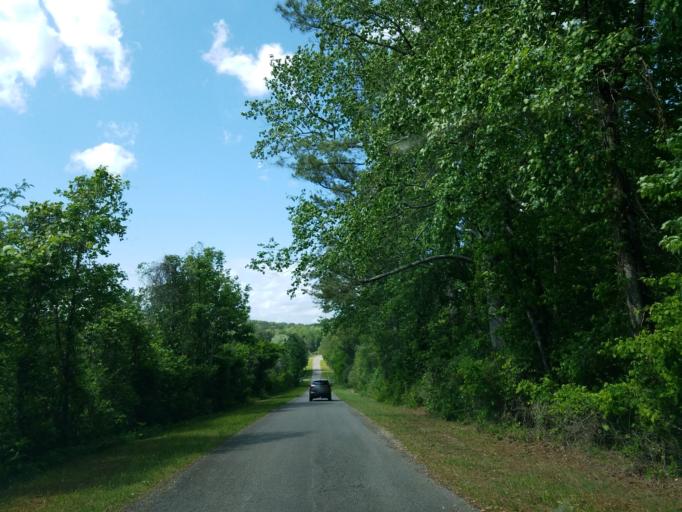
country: US
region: Georgia
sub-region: Cherokee County
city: Ball Ground
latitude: 34.2743
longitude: -84.3121
